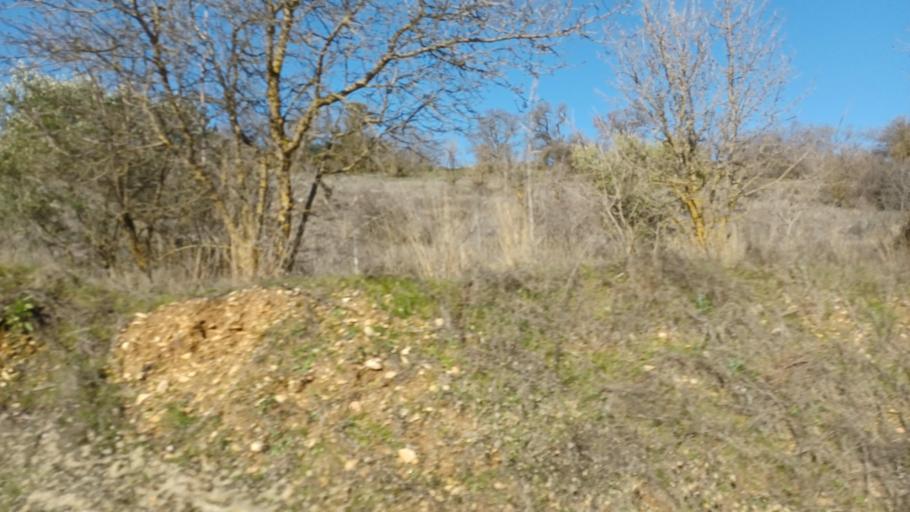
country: CY
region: Limassol
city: Pachna
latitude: 34.8103
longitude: 32.6776
